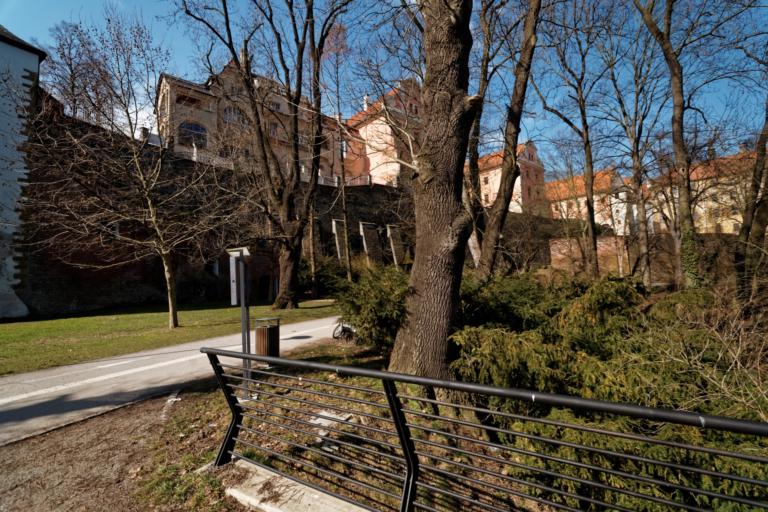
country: CZ
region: Olomoucky
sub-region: Okres Olomouc
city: Olomouc
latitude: 49.5938
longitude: 17.2561
